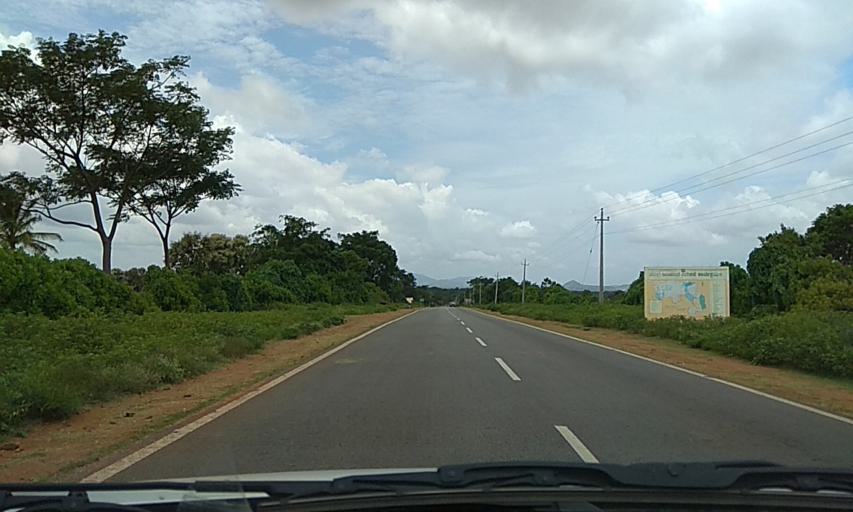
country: IN
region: Karnataka
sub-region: Chamrajnagar
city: Gundlupet
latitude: 11.8146
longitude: 76.7525
